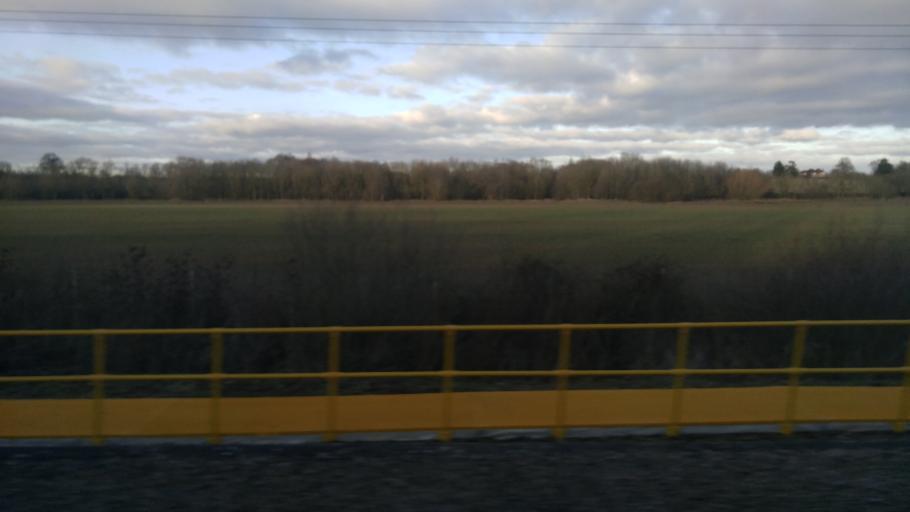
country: GB
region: England
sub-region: Kent
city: Headcorn
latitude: 51.1673
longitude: 0.6065
